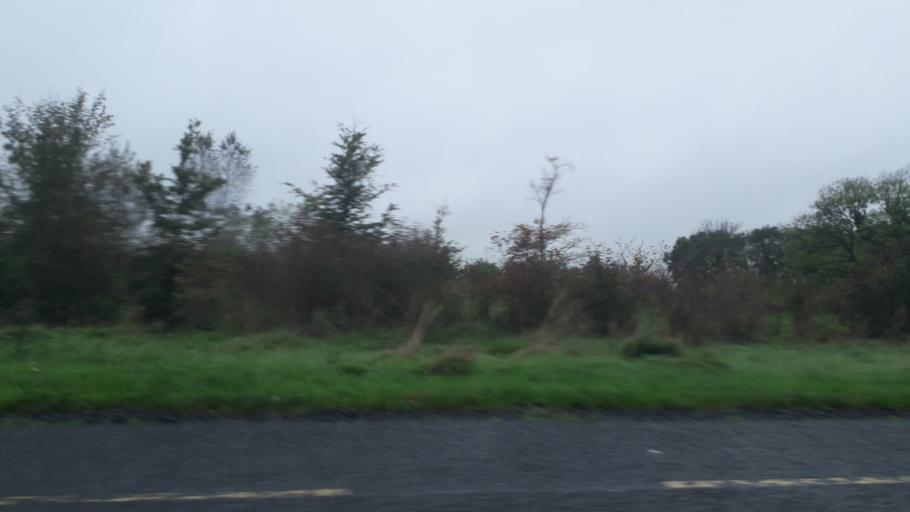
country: IE
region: Leinster
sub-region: An Longfort
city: Edgeworthstown
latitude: 53.6977
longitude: -7.6273
